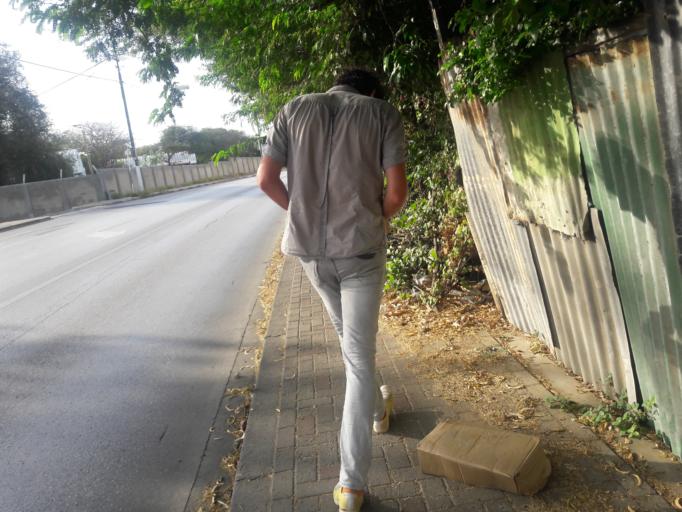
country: CW
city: Willemstad
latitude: 12.1452
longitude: -68.9248
